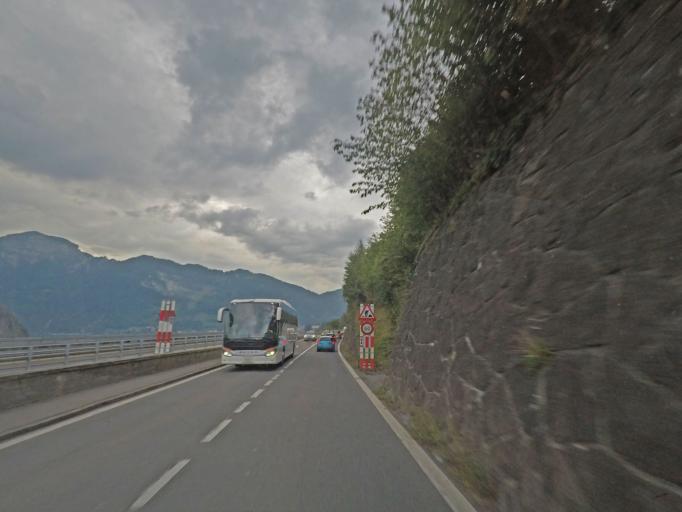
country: CH
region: Schwyz
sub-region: Bezirk Schwyz
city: Ingenbohl
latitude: 46.9741
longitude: 8.6113
